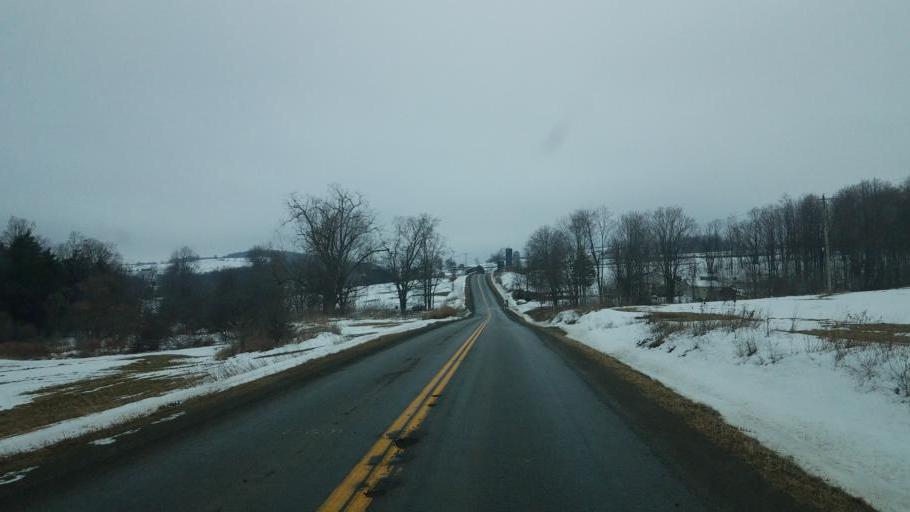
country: US
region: Pennsylvania
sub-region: Tioga County
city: Westfield
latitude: 42.0820
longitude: -77.4873
